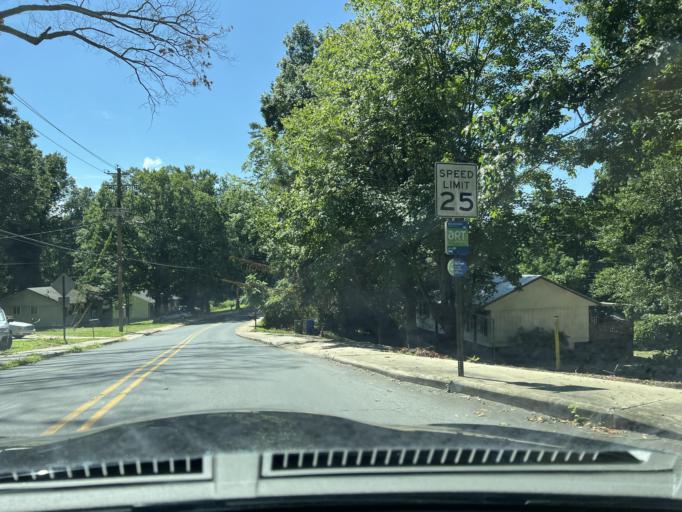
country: US
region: North Carolina
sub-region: Buncombe County
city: Biltmore Forest
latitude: 35.5700
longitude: -82.5141
